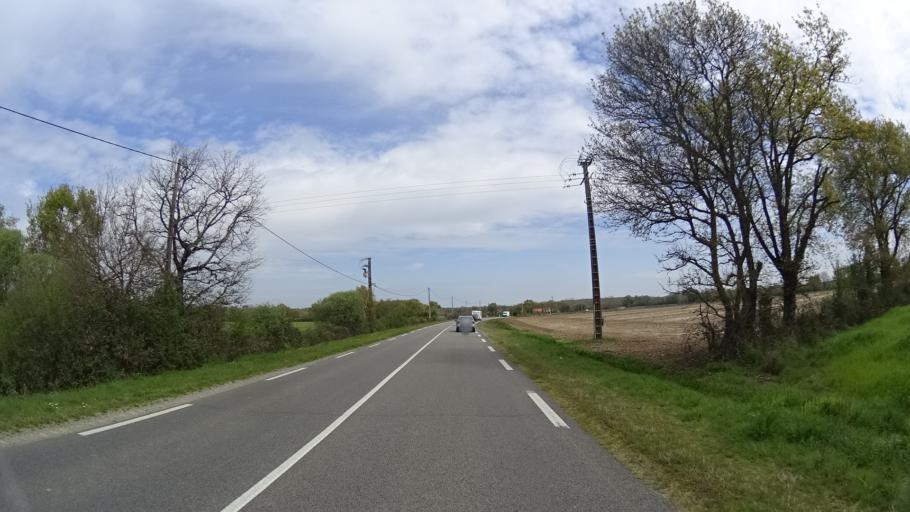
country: FR
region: Pays de la Loire
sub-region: Departement de la Loire-Atlantique
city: Saint-Hilaire-de-Chaleons
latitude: 47.0849
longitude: -1.8577
